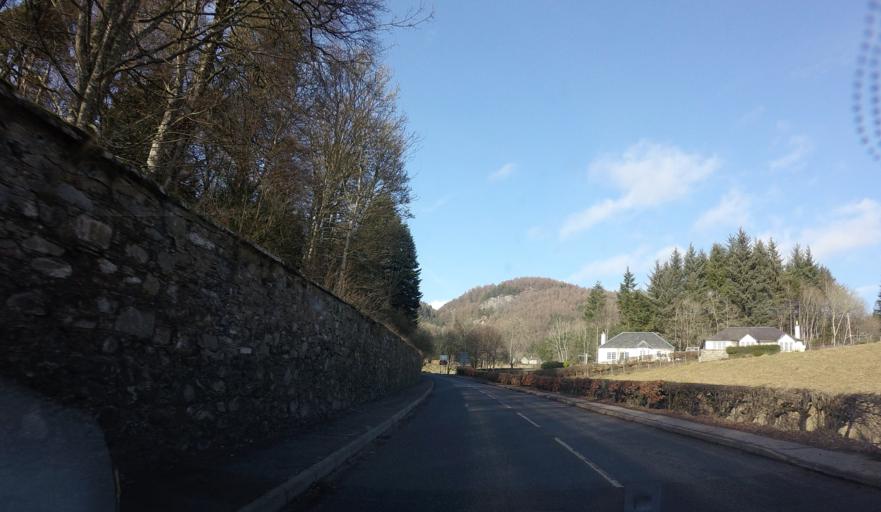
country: GB
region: Scotland
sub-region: Perth and Kinross
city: Bankfoot
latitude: 56.5701
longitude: -3.5901
